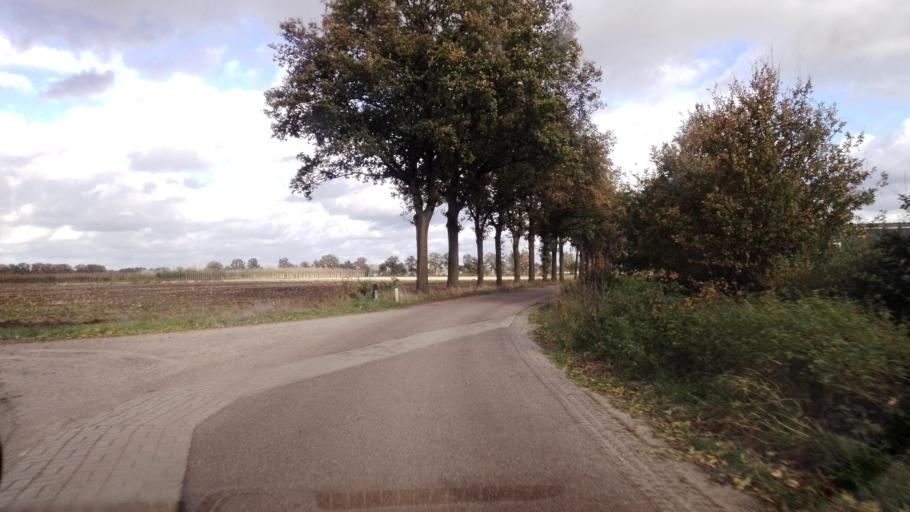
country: NL
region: Limburg
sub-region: Gemeente Venray
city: Venray
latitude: 51.4903
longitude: 5.9386
